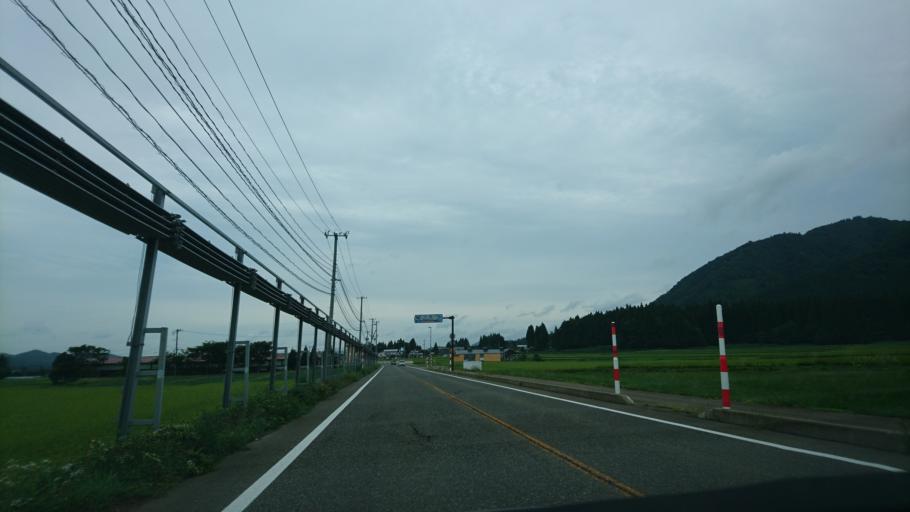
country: JP
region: Akita
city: Yuzawa
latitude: 39.1213
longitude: 140.5781
